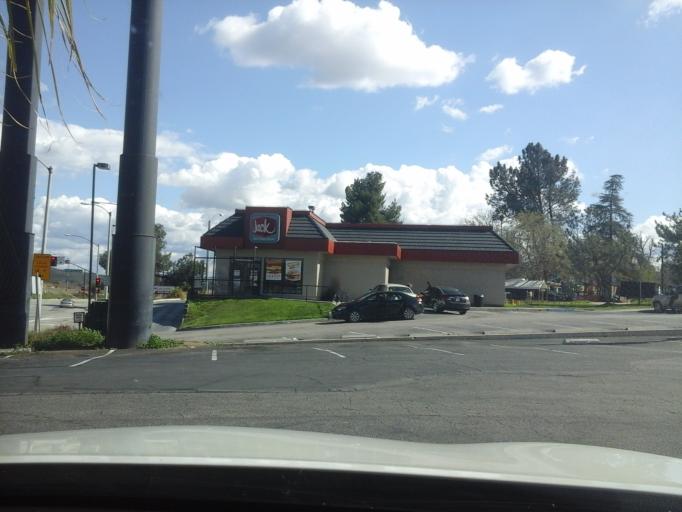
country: US
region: California
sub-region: Los Angeles County
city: Castaic
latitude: 34.4959
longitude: -118.6256
